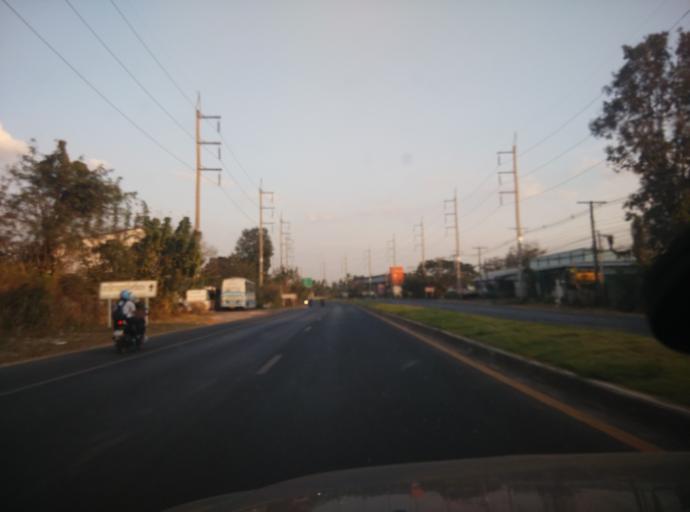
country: TH
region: Sisaket
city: Si Sa Ket
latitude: 15.1280
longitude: 104.2801
